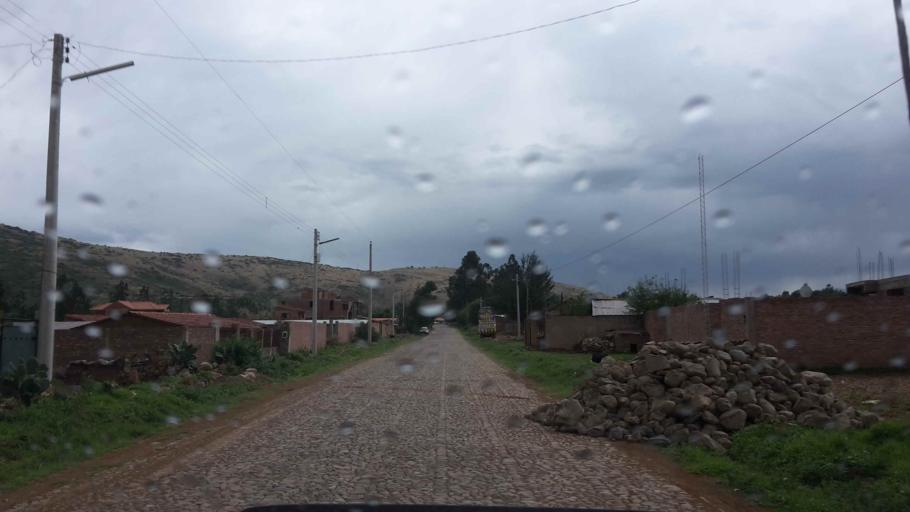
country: BO
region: Cochabamba
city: Tarata
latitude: -17.5496
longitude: -66.1699
